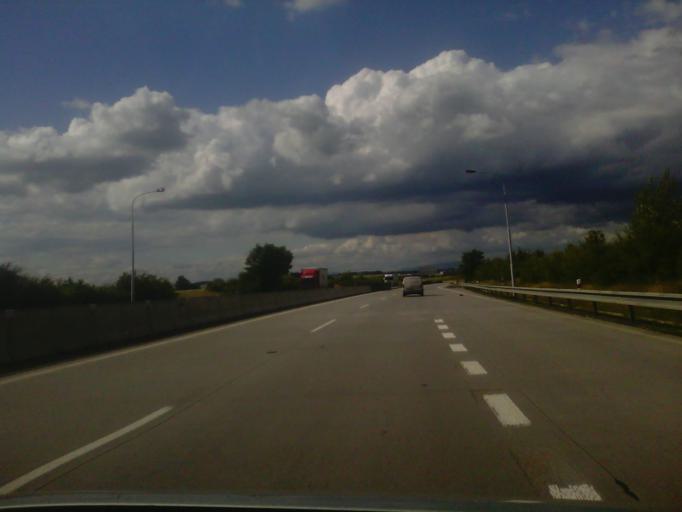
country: CZ
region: Olomoucky
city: Hnevotin
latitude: 49.5762
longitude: 17.2089
